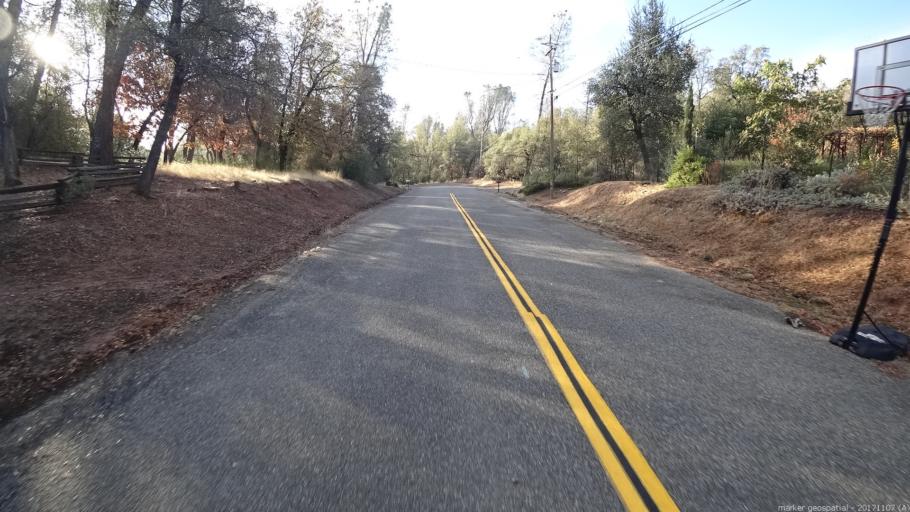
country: US
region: California
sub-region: Shasta County
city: Shasta
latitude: 40.5782
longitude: -122.4671
